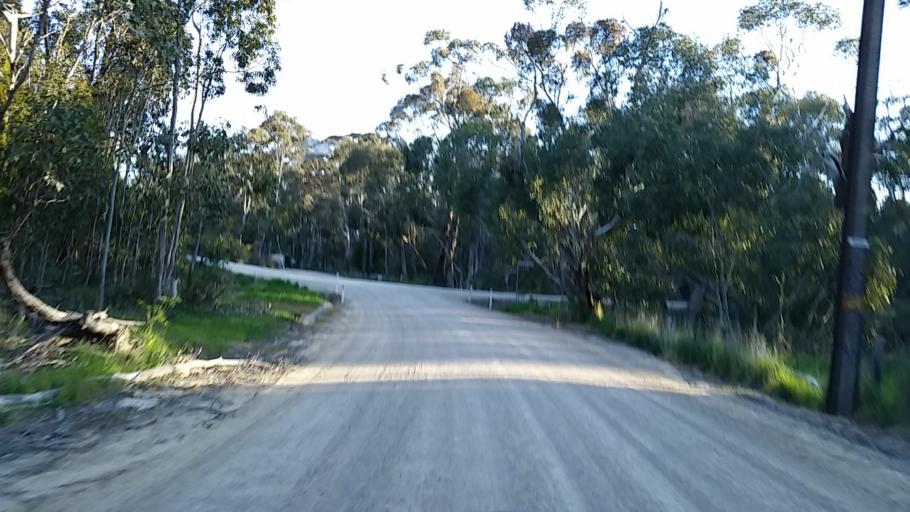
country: AU
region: South Australia
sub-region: Alexandrina
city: Mount Compass
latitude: -35.2731
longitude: 138.7015
